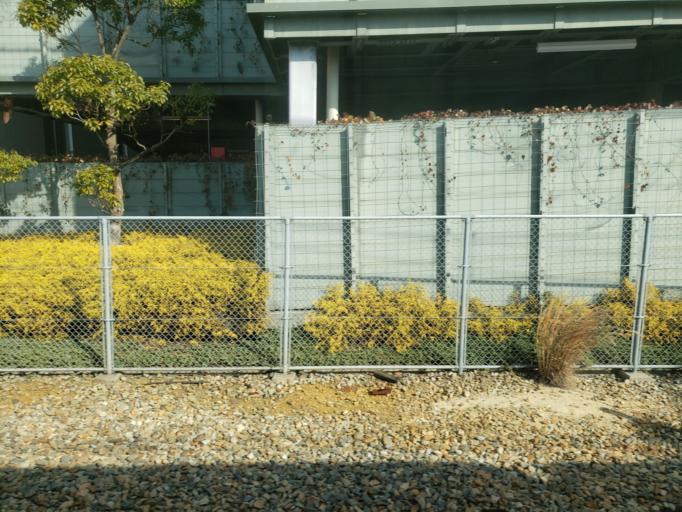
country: JP
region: Hyogo
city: Amagasaki
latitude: 34.7325
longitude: 135.4294
